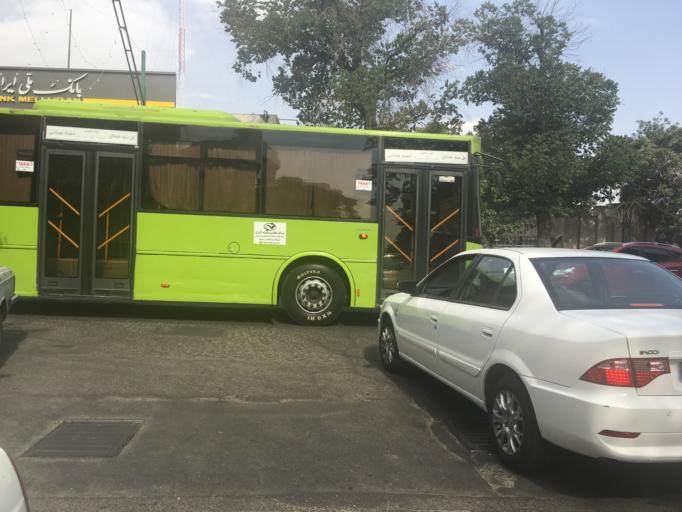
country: IR
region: Tehran
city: Tehran
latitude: 35.7341
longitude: 51.4452
